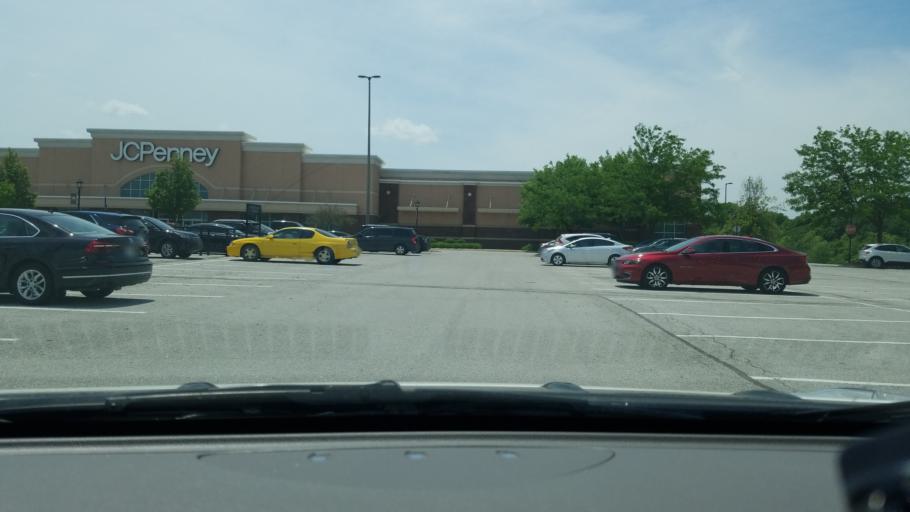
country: US
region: Nebraska
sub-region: Sarpy County
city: Papillion
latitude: 41.1345
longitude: -96.0304
